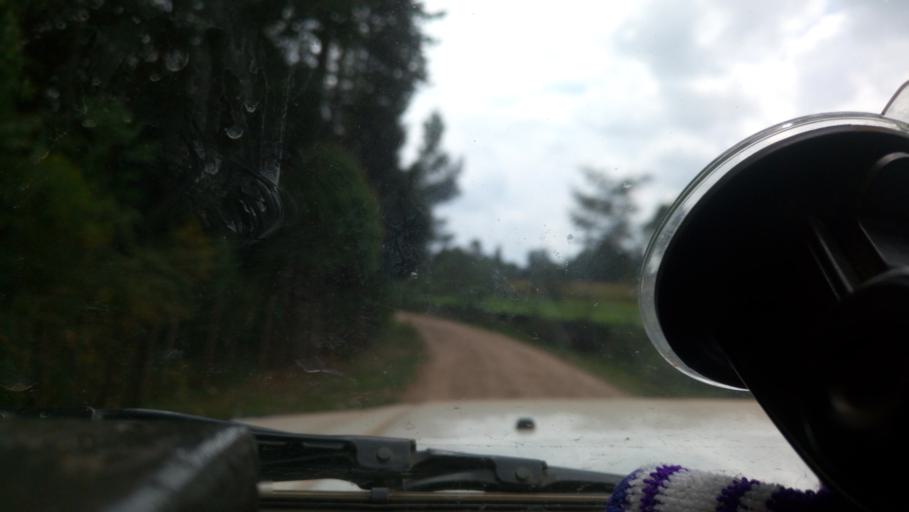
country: KE
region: Kericho
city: Sotik
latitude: -0.6165
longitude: 35.1240
